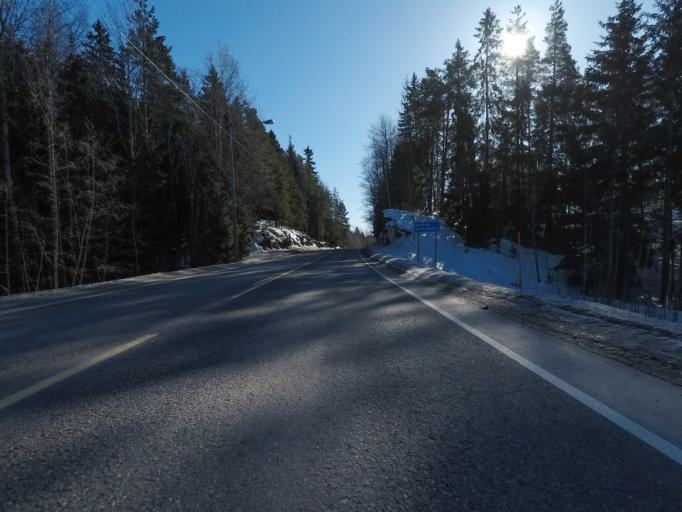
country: FI
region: Uusimaa
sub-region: Helsinki
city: Espoo
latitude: 60.2406
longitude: 24.5910
